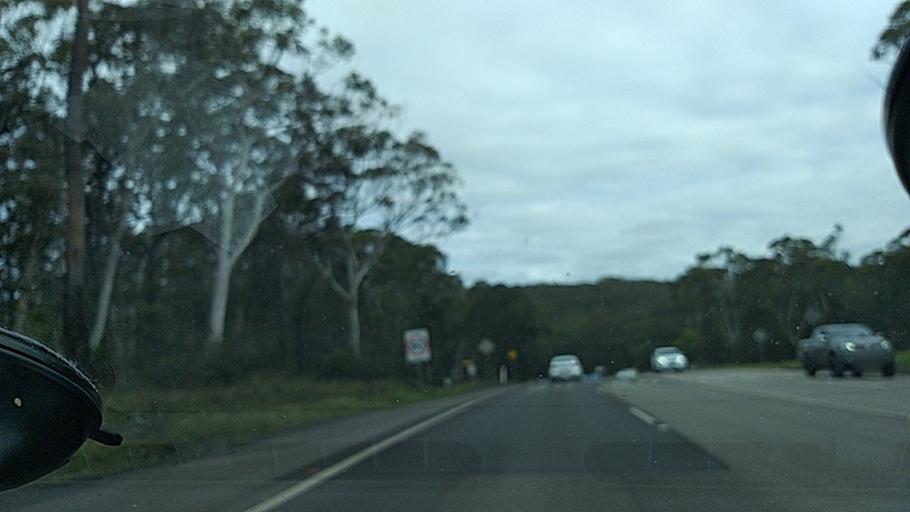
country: AU
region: New South Wales
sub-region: Wollondilly
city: Douglas Park
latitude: -34.2081
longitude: 150.7949
